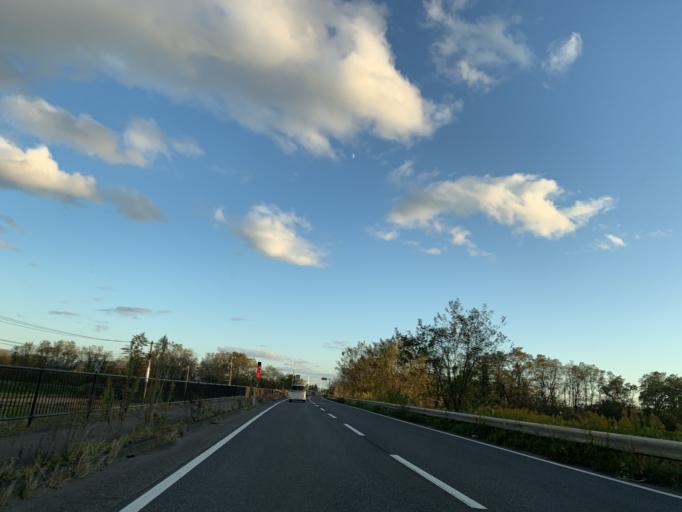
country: JP
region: Iwate
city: Mizusawa
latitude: 39.1887
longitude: 141.1174
